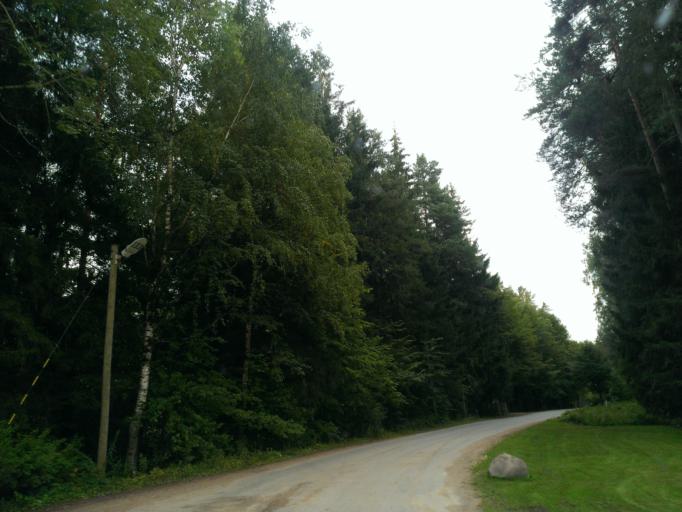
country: LV
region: Ogre
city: Ogre
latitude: 56.8279
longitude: 24.5828
